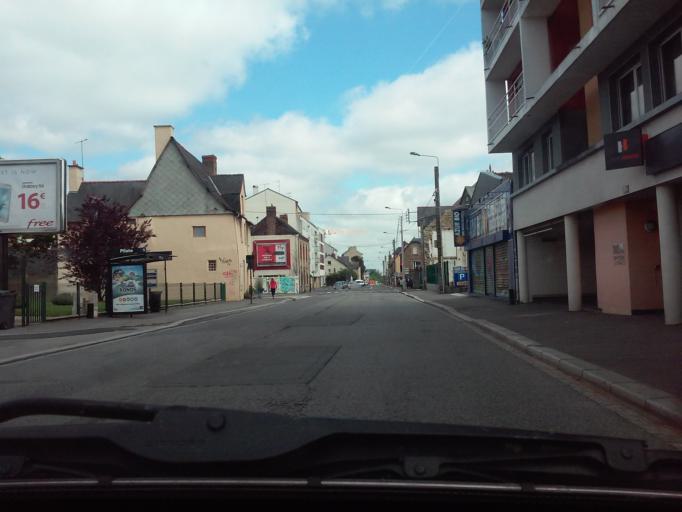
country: FR
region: Brittany
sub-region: Departement d'Ille-et-Vilaine
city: Rennes
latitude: 48.0938
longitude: -1.6907
